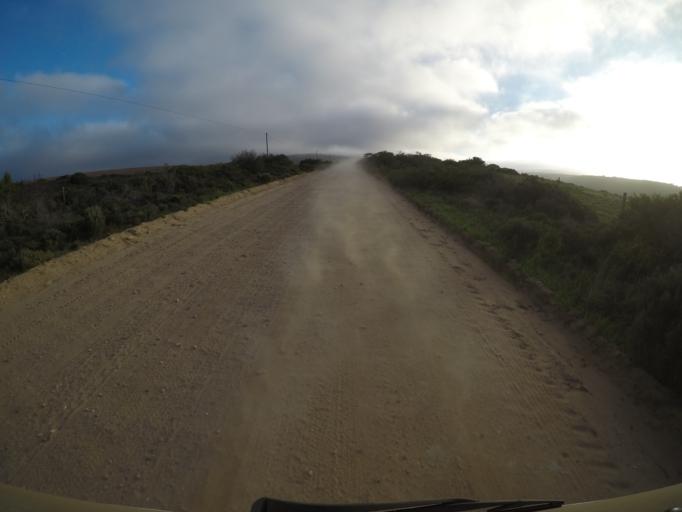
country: ZA
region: Western Cape
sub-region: Eden District Municipality
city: Mossel Bay
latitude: -34.1333
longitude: 22.0439
